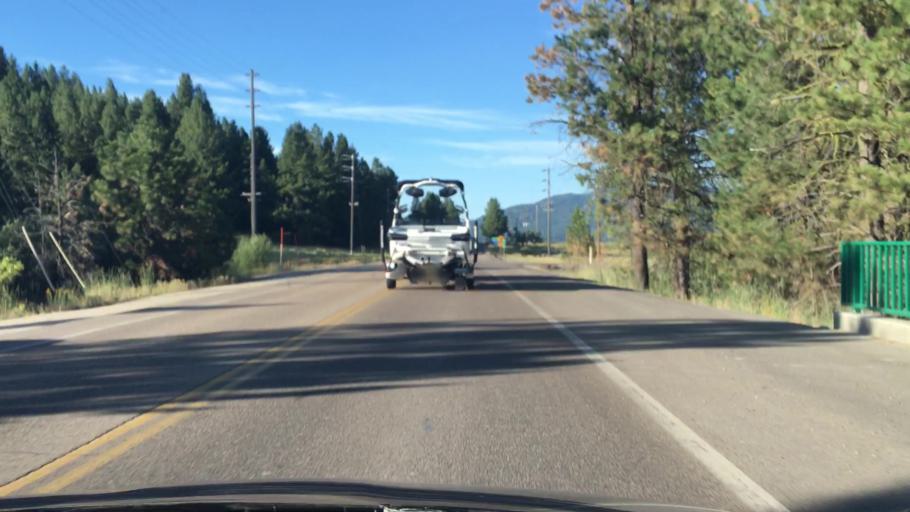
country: US
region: Idaho
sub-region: Valley County
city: Cascade
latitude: 44.5247
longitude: -116.0439
